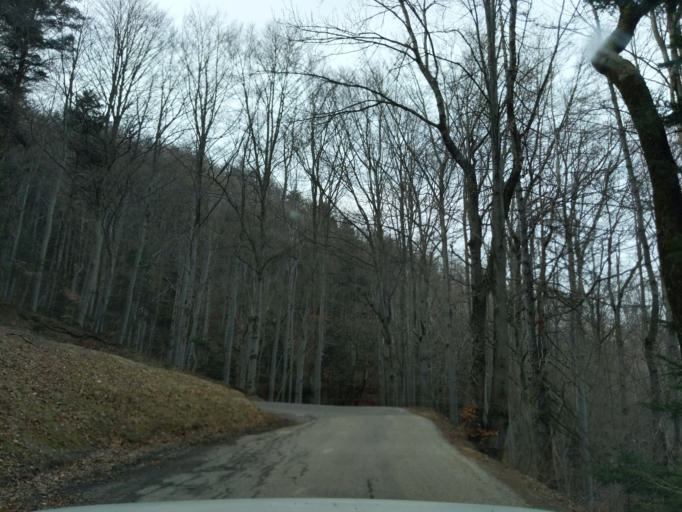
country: FR
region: Rhone-Alpes
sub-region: Departement de la Savoie
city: Villargondran
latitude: 45.2560
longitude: 6.3635
